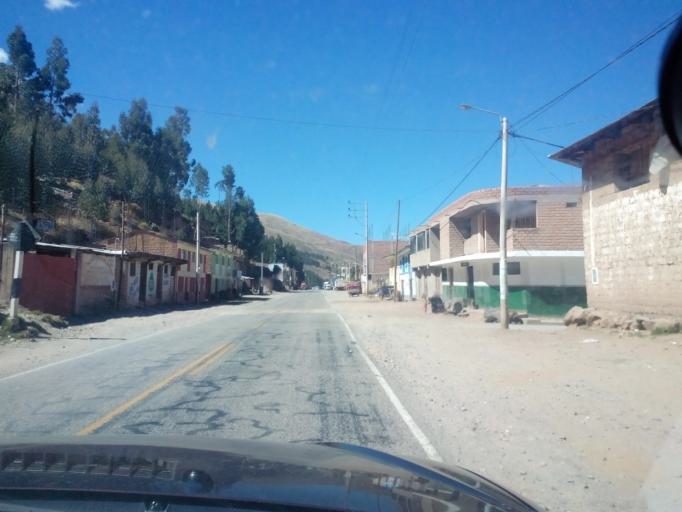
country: PE
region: Cusco
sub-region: Provincia de Canchis
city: Combapata
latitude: -14.0998
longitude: -71.4297
